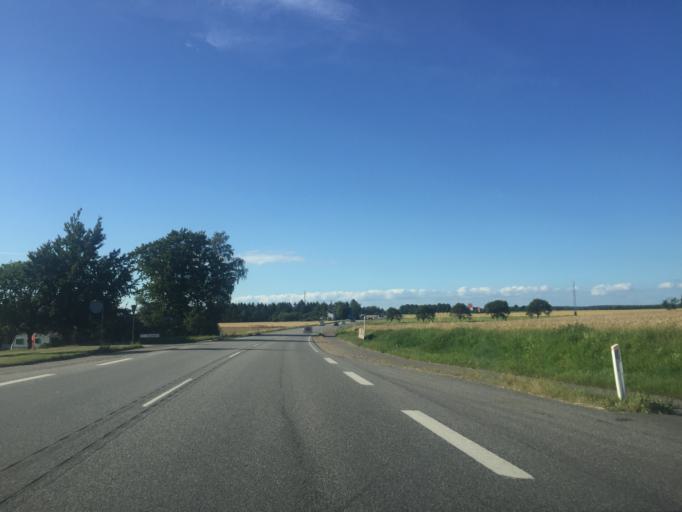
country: DK
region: Zealand
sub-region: Guldborgsund Kommune
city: Norre Alslev
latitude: 54.8381
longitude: 11.8597
